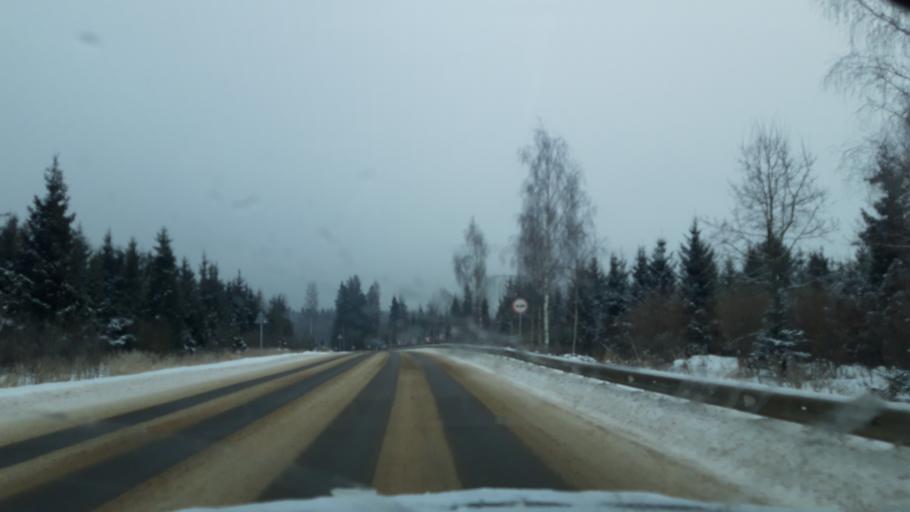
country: RU
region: Moskovskaya
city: Avtopoligon
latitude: 56.2633
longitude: 37.2663
